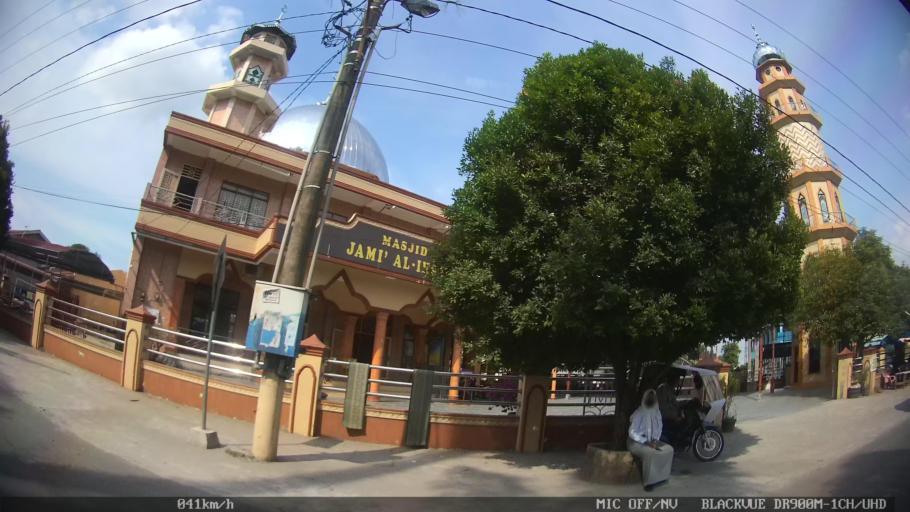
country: ID
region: North Sumatra
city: Binjai
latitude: 3.6275
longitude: 98.4941
